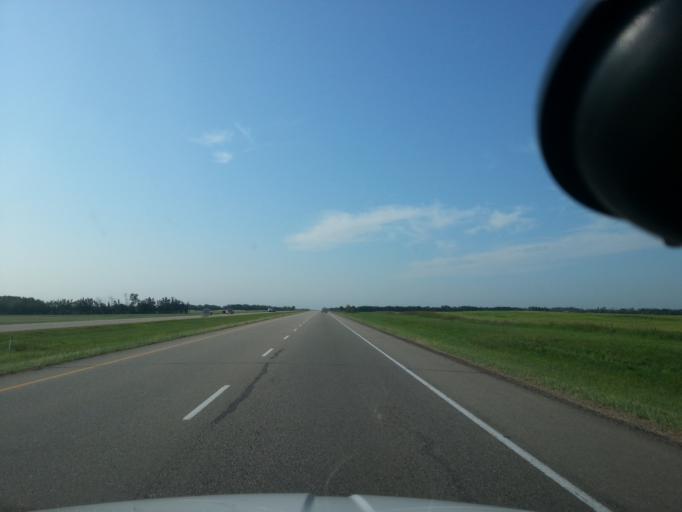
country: CA
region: Alberta
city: Ponoka
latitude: 52.8250
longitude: -113.6442
